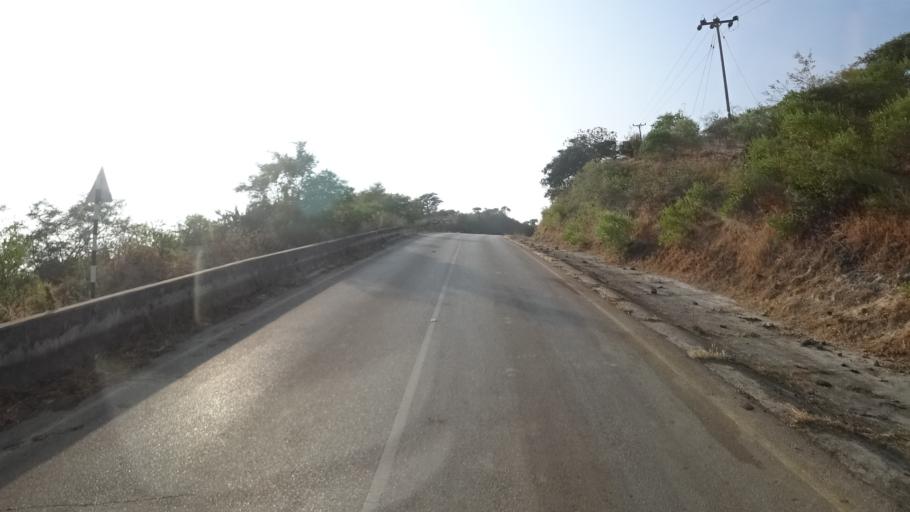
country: YE
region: Al Mahrah
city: Hawf
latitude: 16.7422
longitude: 53.3631
